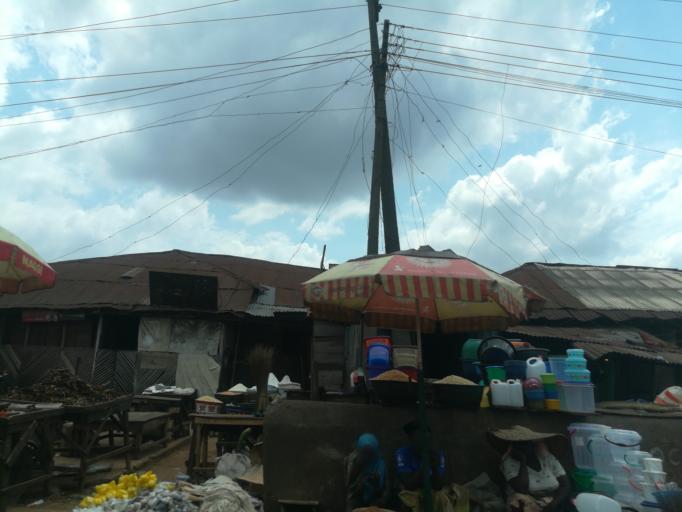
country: NG
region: Oyo
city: Ibadan
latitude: 7.3878
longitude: 3.9068
